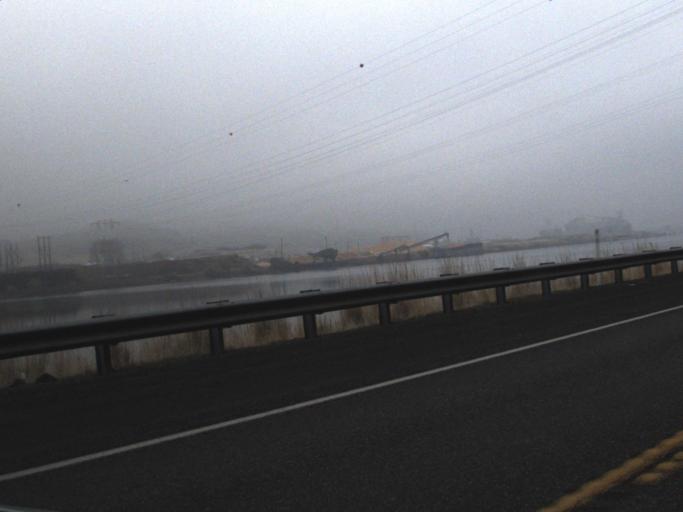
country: US
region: Washington
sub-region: Asotin County
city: Clarkston Heights-Vineland
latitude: 46.4193
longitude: -117.1109
